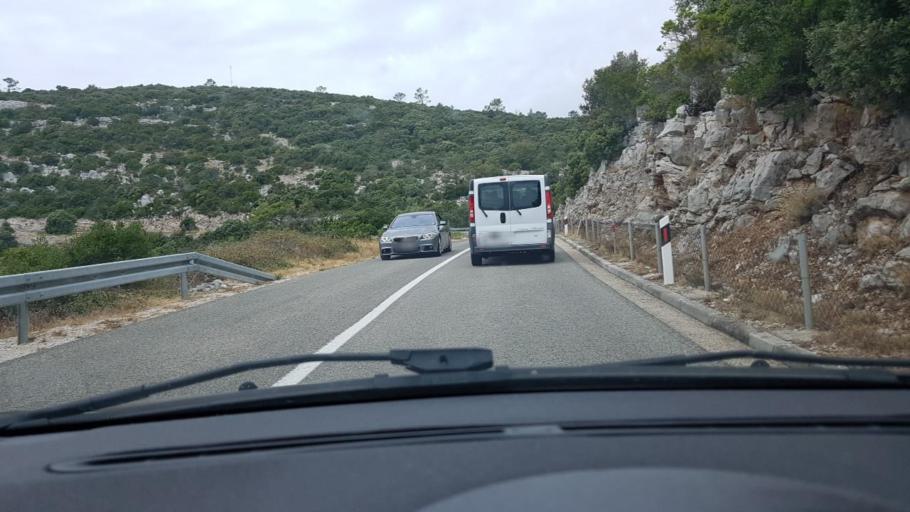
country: HR
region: Dubrovacko-Neretvanska
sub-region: Grad Korcula
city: Zrnovo
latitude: 42.9379
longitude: 17.0200
